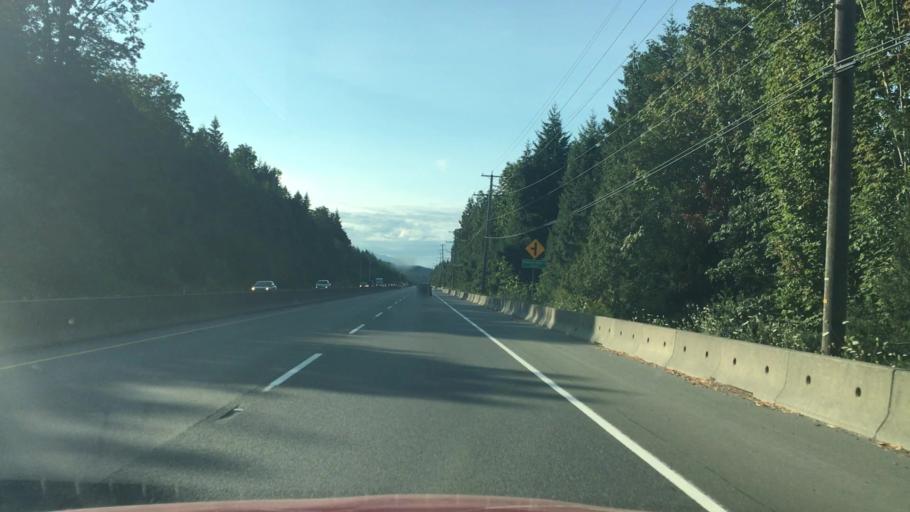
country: CA
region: British Columbia
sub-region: Cowichan Valley Regional District
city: Ladysmith
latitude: 48.9294
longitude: -123.7537
